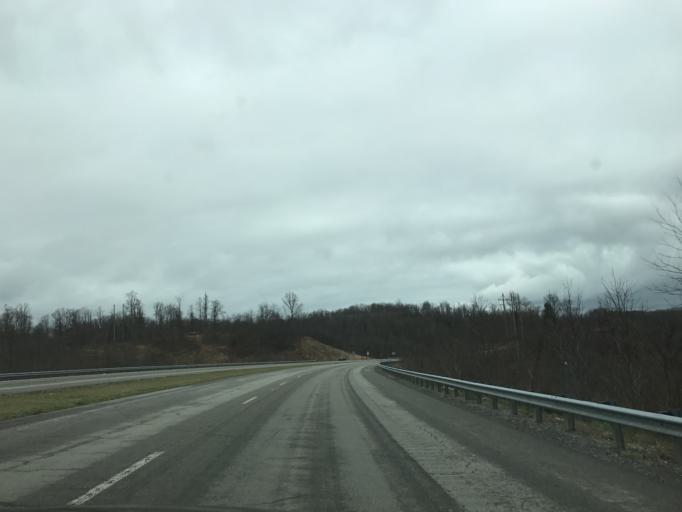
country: US
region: West Virginia
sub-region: Raleigh County
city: Sophia
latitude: 37.7173
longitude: -81.2822
